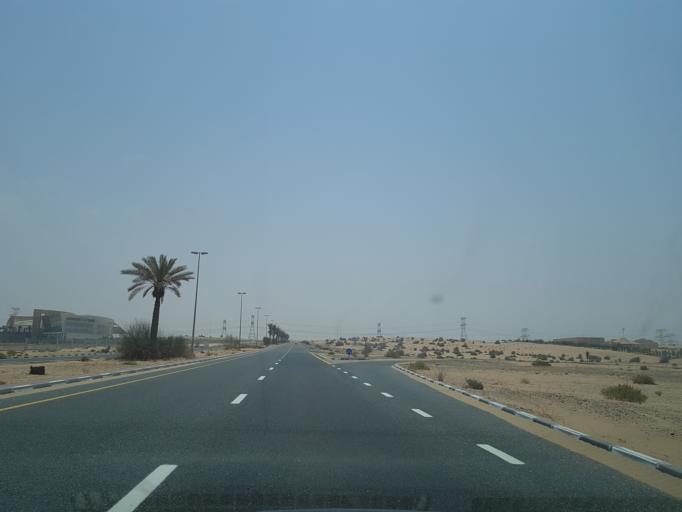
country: AE
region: Ash Shariqah
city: Sharjah
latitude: 25.1090
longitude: 55.4097
